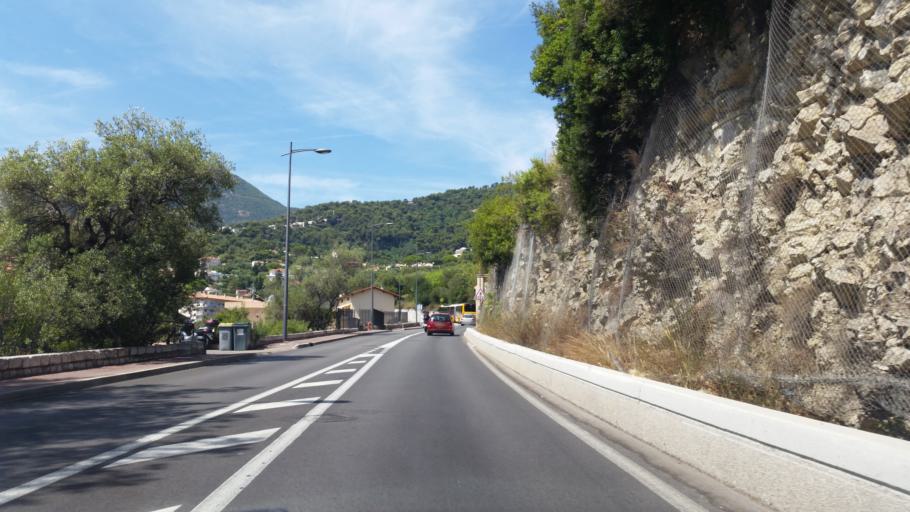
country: FR
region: Provence-Alpes-Cote d'Azur
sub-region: Departement des Alpes-Maritimes
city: Roquebrune-Cap-Martin
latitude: 43.7606
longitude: 7.4754
